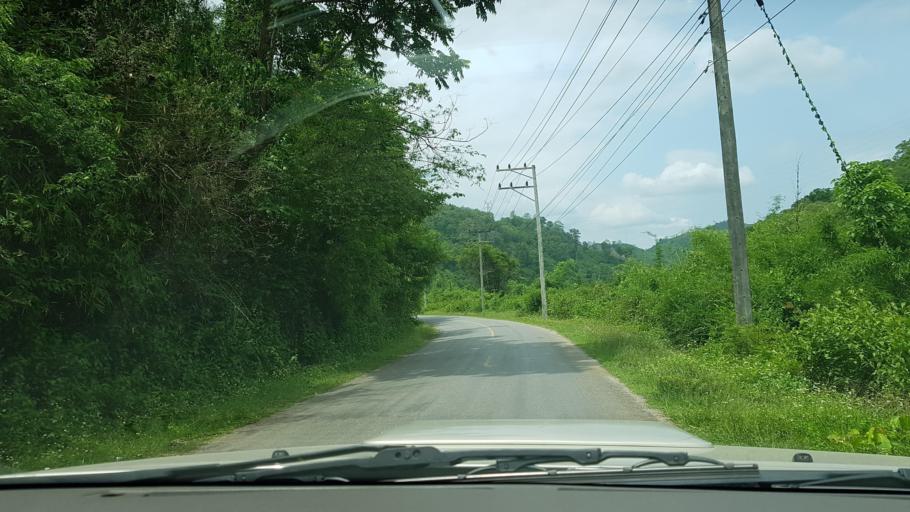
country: TH
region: Nan
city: Chaloem Phra Kiat
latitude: 19.9554
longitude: 101.2559
